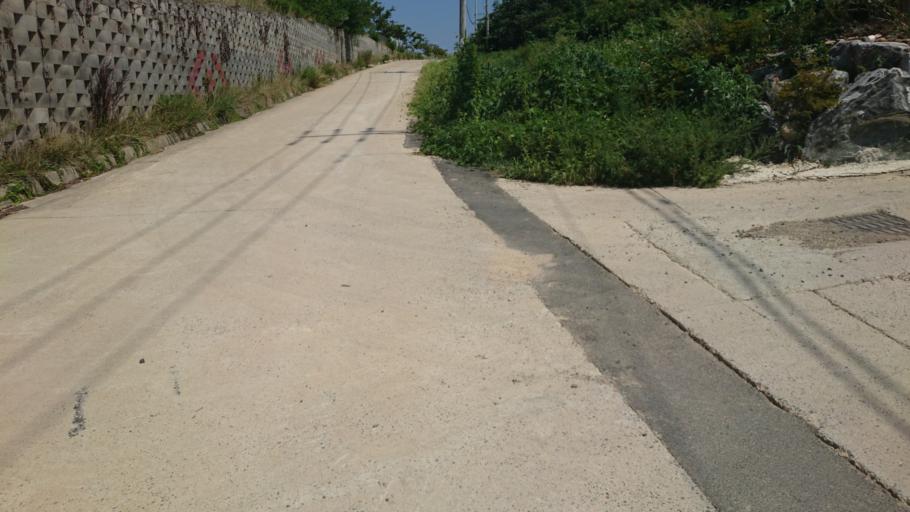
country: KR
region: Gyeongsangbuk-do
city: Gyeongsan-si
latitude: 35.8295
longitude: 128.6702
